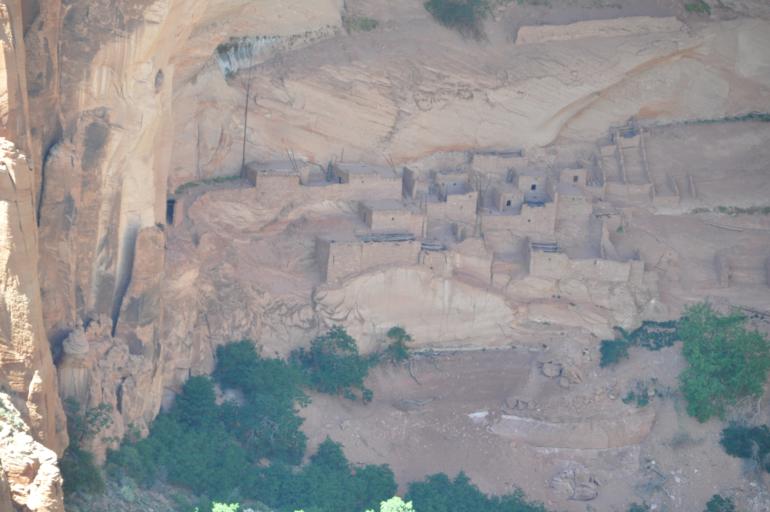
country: US
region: Arizona
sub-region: Navajo County
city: Kayenta
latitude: 36.6806
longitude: -110.5342
